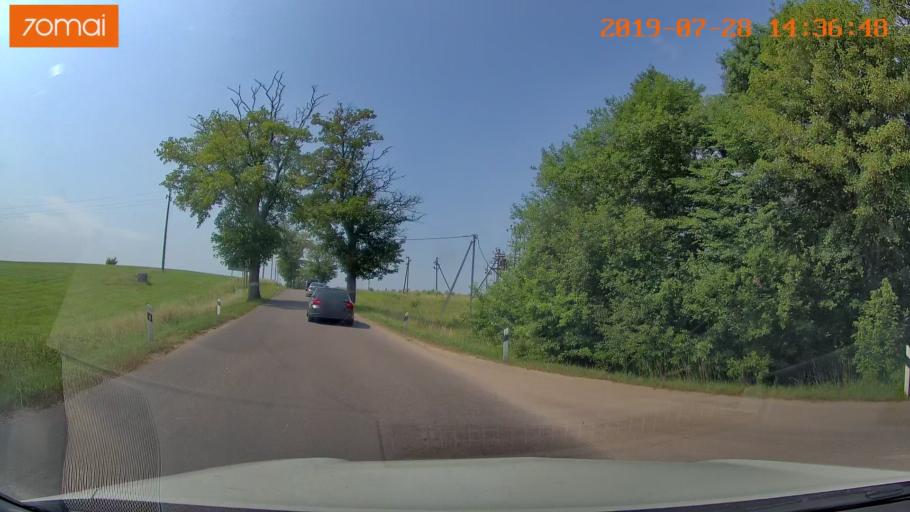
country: RU
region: Kaliningrad
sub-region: Gorod Kaliningrad
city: Yantarnyy
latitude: 54.8397
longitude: 20.0056
